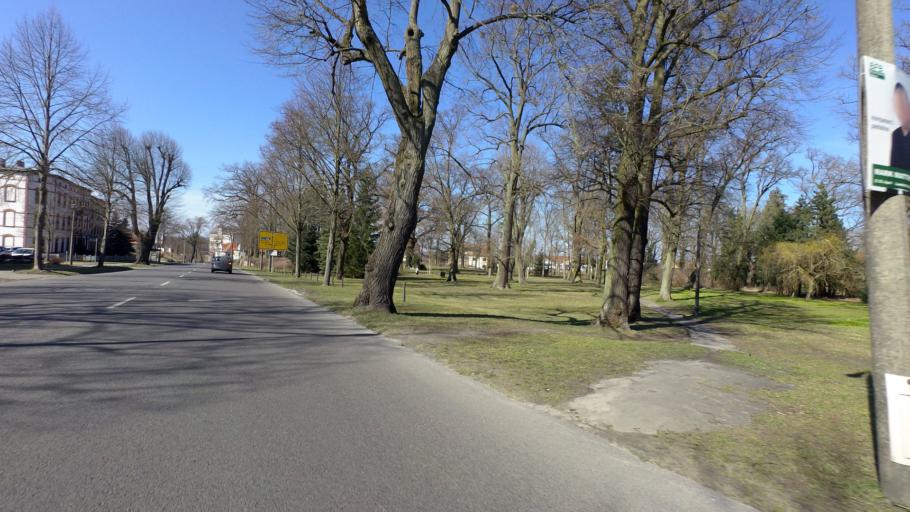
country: DE
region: Brandenburg
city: Eberswalde
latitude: 52.8279
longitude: 13.8299
